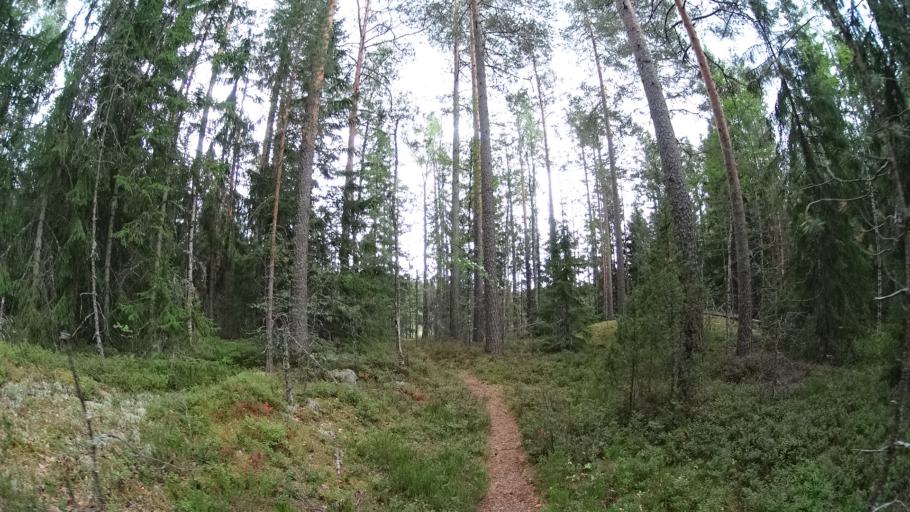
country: FI
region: Uusimaa
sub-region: Helsinki
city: Espoo
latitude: 60.3069
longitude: 24.5742
